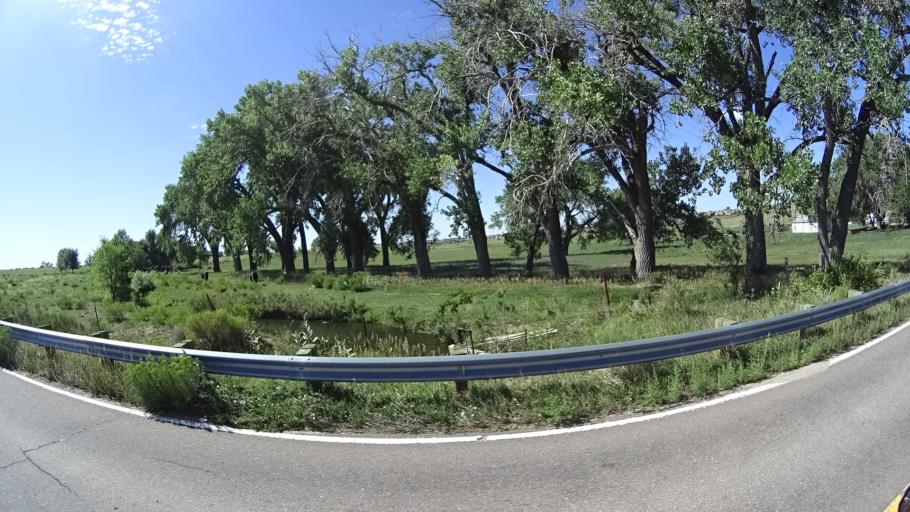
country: US
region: Colorado
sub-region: El Paso County
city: Security-Widefield
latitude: 38.7375
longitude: -104.6635
